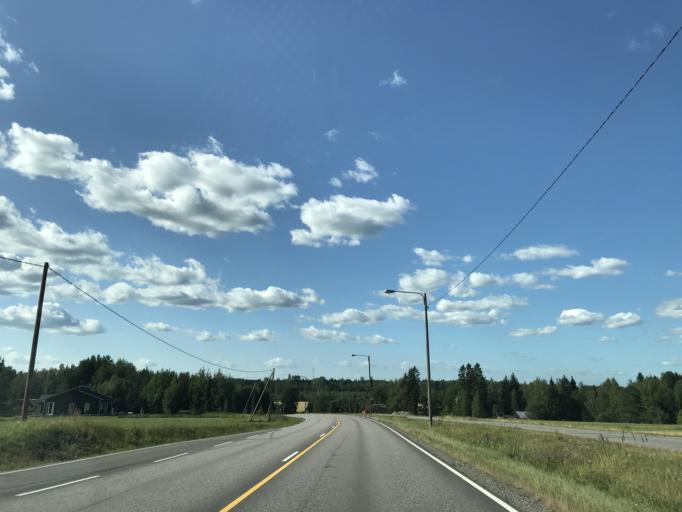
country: FI
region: Uusimaa
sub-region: Helsinki
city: Nurmijaervi
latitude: 60.4313
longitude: 24.8541
